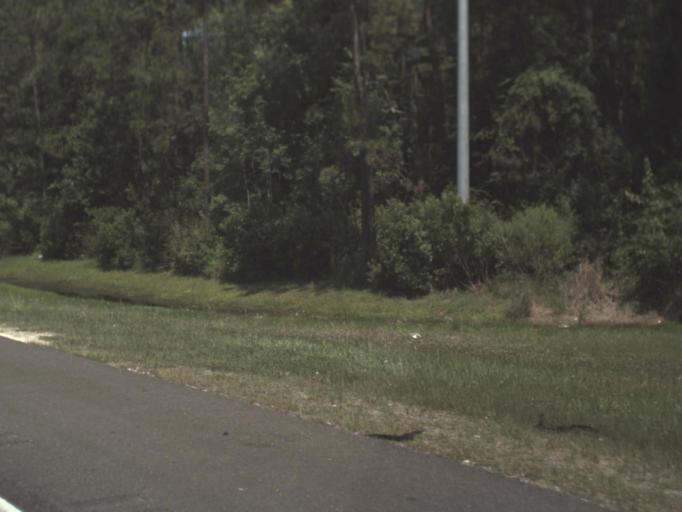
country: US
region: Florida
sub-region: Duval County
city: Baldwin
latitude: 30.3059
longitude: -81.8866
